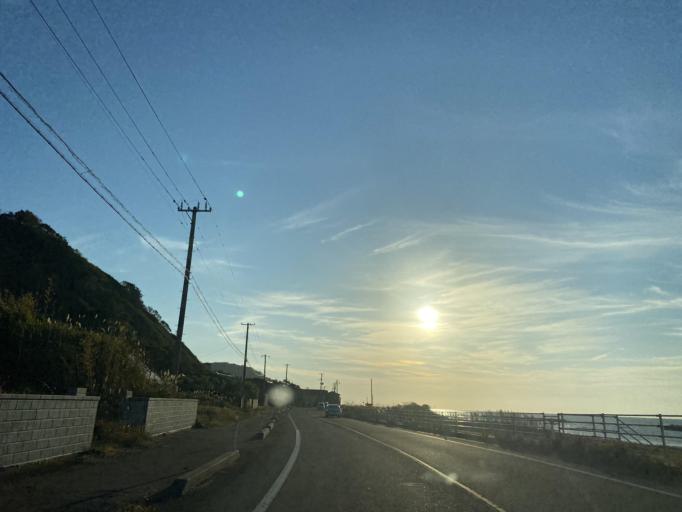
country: JP
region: Niigata
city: Kashiwazaki
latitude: 37.4966
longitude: 138.6378
